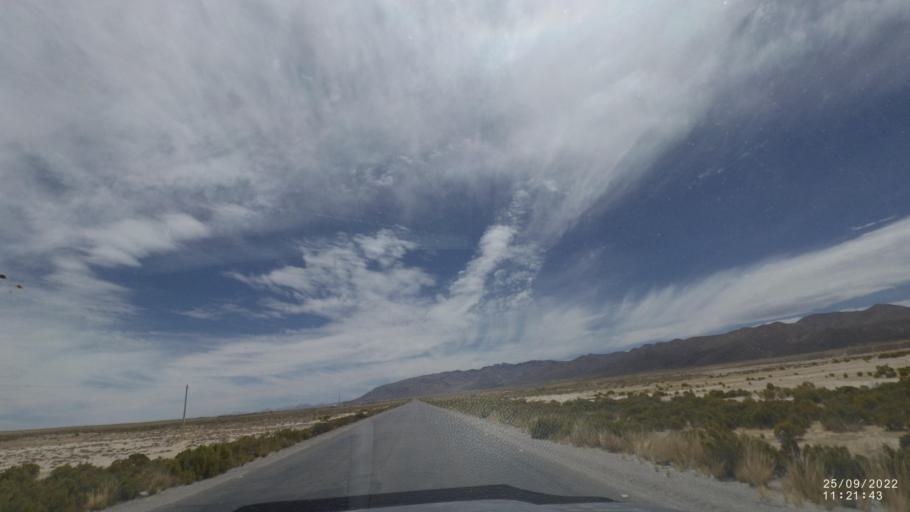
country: BO
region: Oruro
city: Challapata
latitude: -19.1387
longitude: -66.7699
